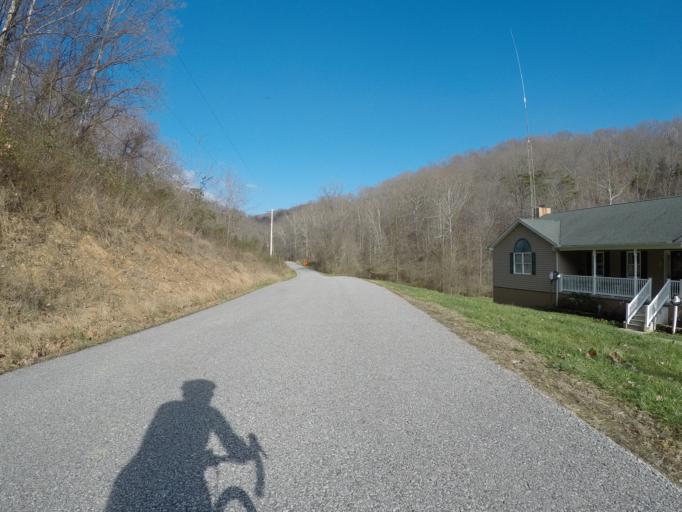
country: US
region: West Virginia
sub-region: Cabell County
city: Pea Ridge
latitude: 38.4237
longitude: -82.3418
